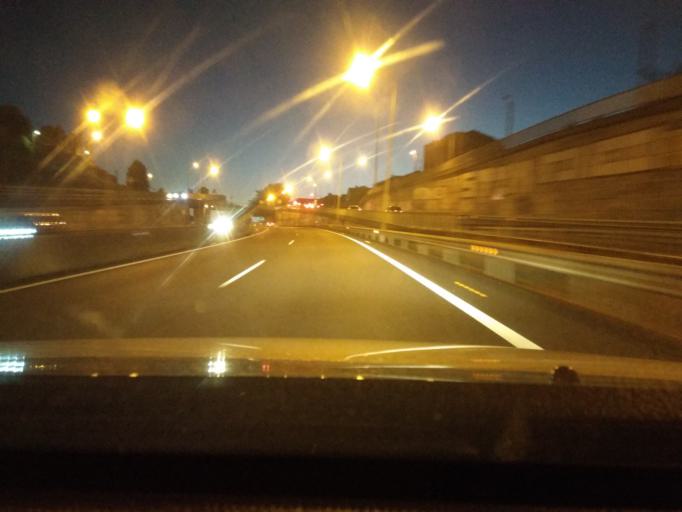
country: ES
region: Galicia
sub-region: Provincia de Pontevedra
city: Vigo
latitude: 42.2492
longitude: -8.6923
